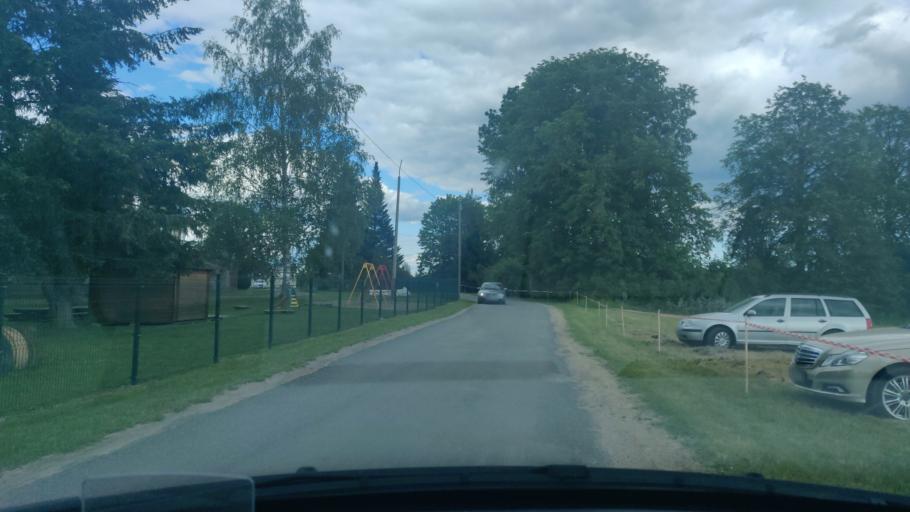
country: EE
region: Jogevamaa
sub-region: Mustvee linn
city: Mustvee
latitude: 58.9840
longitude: 26.8689
